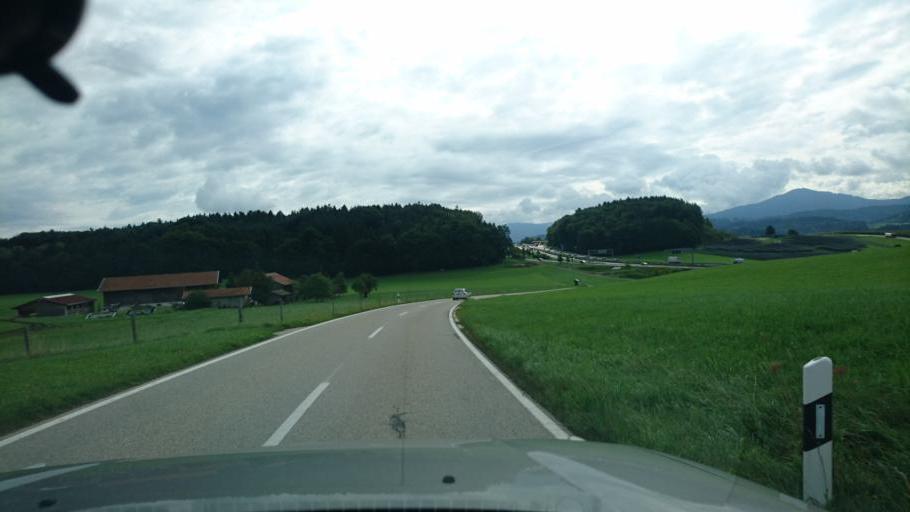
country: DE
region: Bavaria
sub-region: Upper Bavaria
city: Bergen
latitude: 47.8295
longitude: 12.5787
